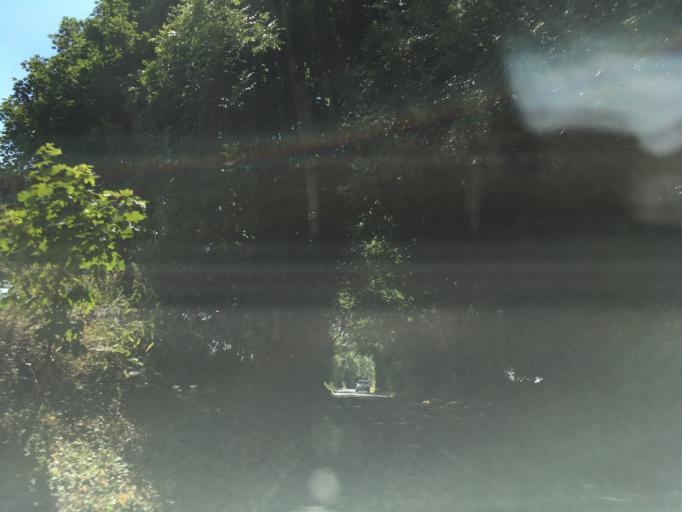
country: GB
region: England
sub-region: Gloucestershire
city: Chalford
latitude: 51.7466
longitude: -2.1386
